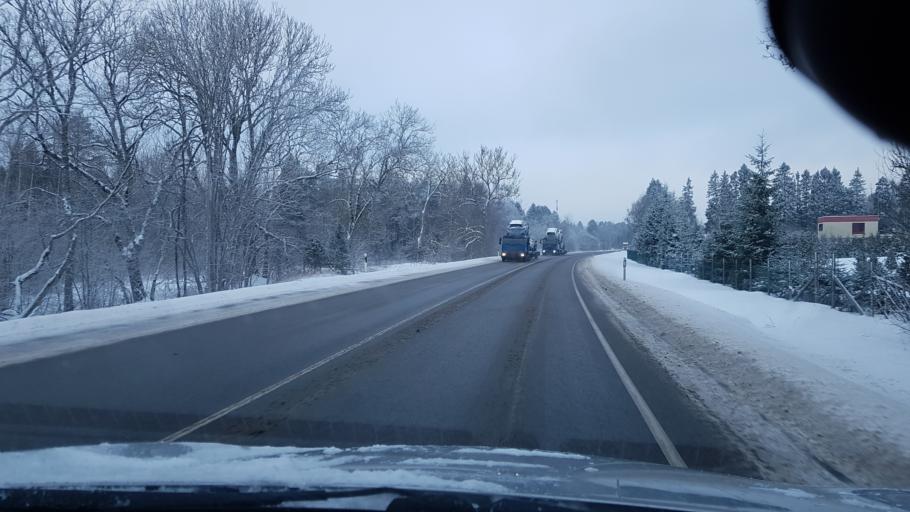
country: EE
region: Harju
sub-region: Keila linn
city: Keila
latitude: 59.3377
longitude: 24.2747
